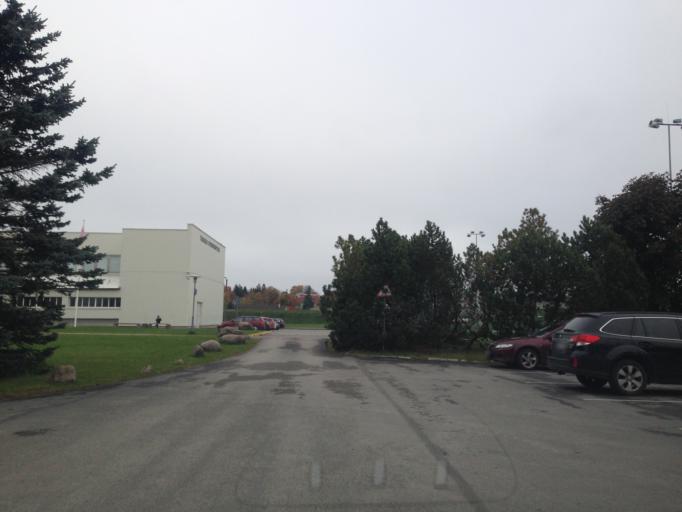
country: EE
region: Harju
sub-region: Harku vald
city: Tabasalu
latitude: 59.4272
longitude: 24.5347
